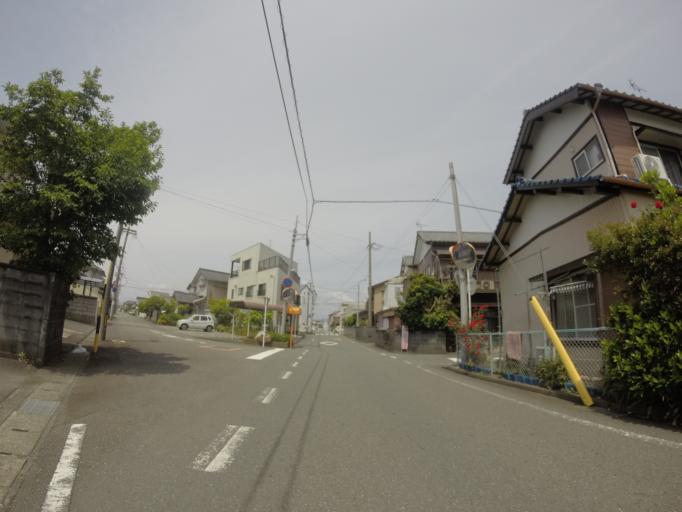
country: JP
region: Shizuoka
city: Yaizu
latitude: 34.8441
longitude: 138.3284
